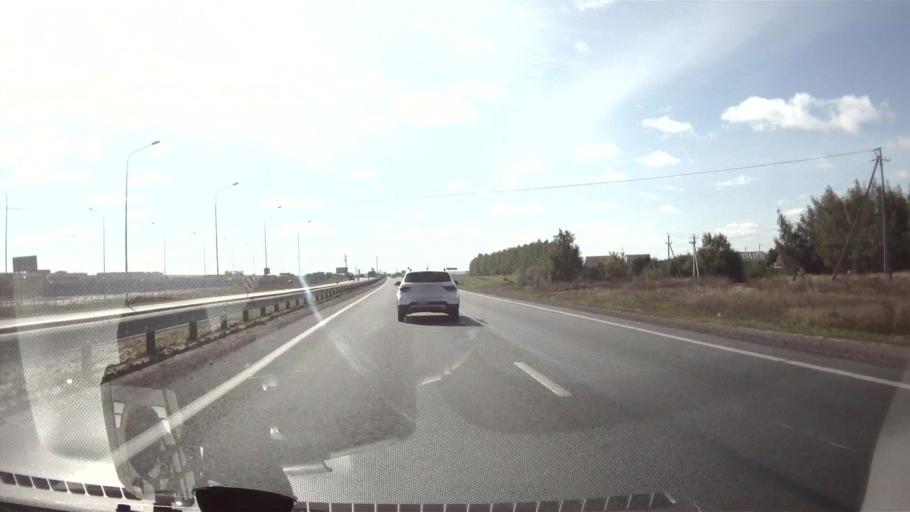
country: RU
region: Ulyanovsk
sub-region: Ulyanovskiy Rayon
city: Ulyanovsk
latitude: 54.2814
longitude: 48.2585
